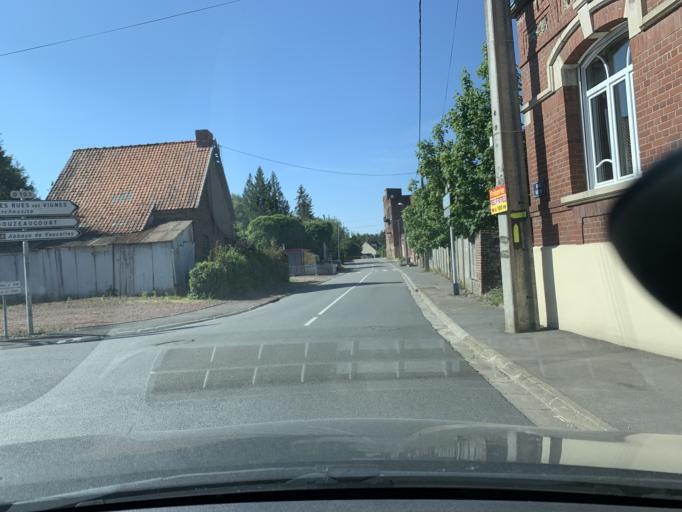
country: FR
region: Nord-Pas-de-Calais
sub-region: Departement du Nord
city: Rumilly-en-Cambresis
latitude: 50.1061
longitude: 3.2485
